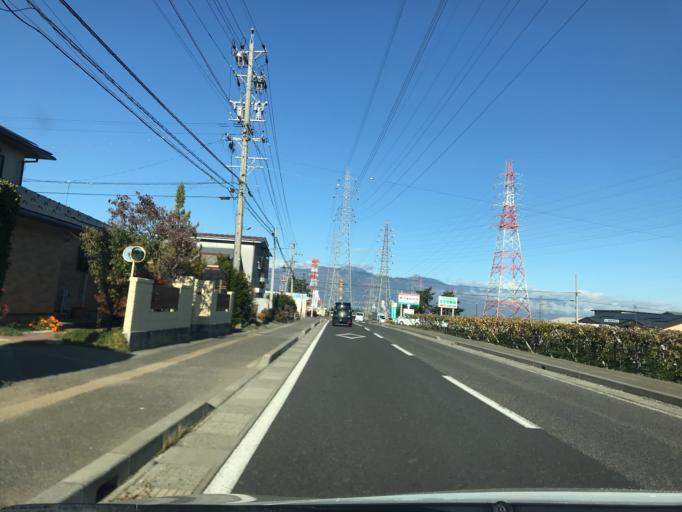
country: JP
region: Nagano
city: Shiojiri
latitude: 36.1241
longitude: 137.9383
